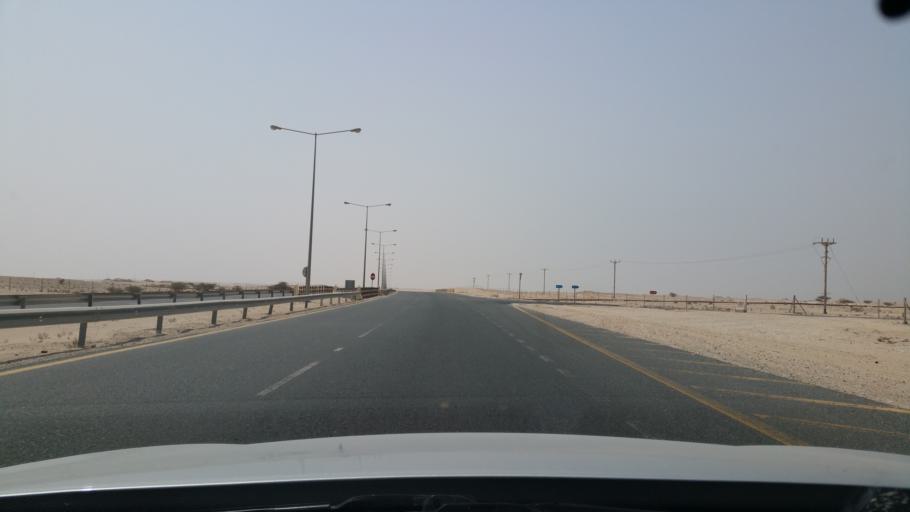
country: QA
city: Umm Bab
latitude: 25.2016
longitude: 50.8041
